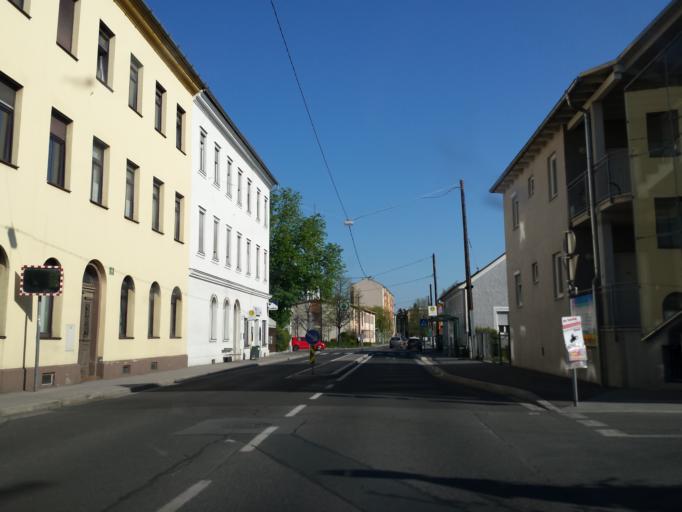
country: AT
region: Styria
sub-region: Graz Stadt
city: Goesting
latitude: 47.0884
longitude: 15.4176
